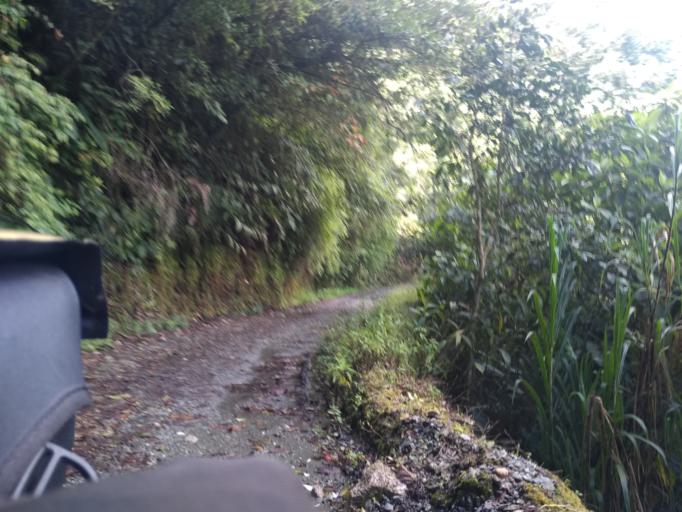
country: EC
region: Tungurahua
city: Banos
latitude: -1.4046
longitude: -78.2774
